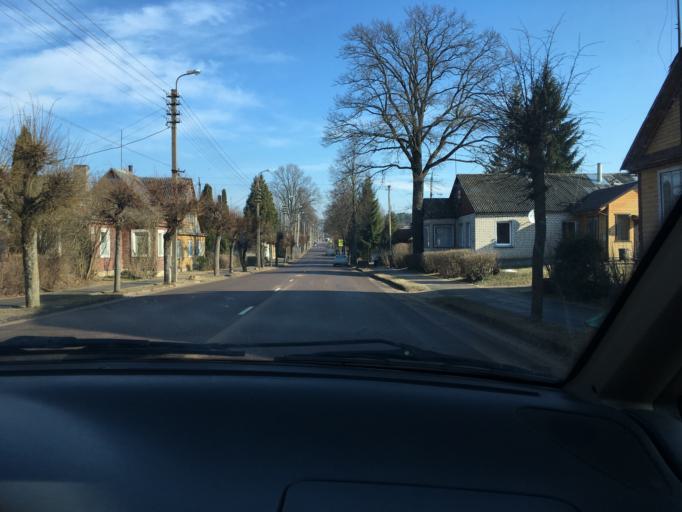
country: LT
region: Panevezys
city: Rokiskis
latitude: 55.7482
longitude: 25.8418
